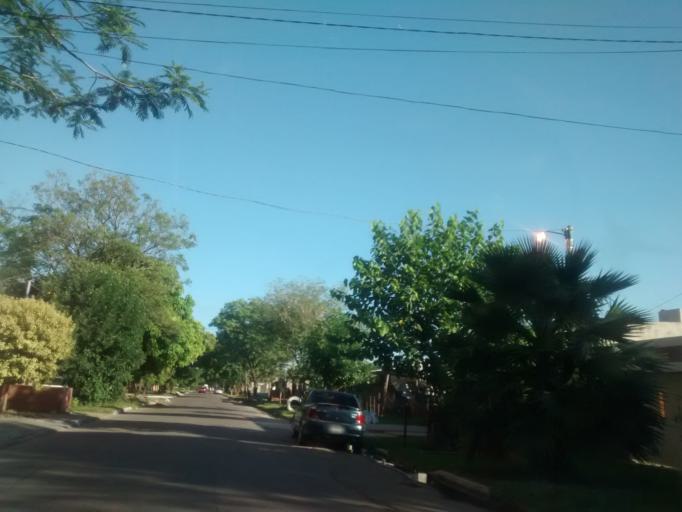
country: AR
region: Chaco
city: Resistencia
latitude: -27.4613
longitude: -58.9828
